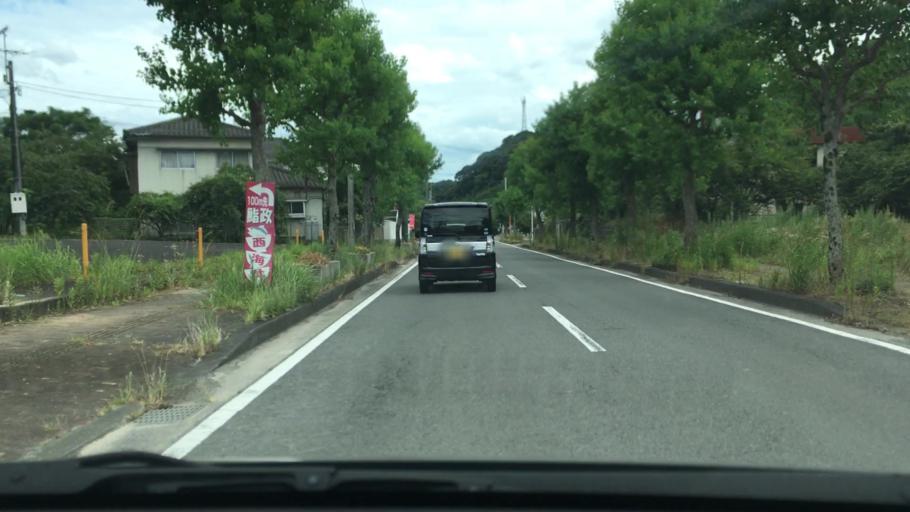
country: JP
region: Nagasaki
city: Sasebo
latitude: 32.9898
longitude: 129.7653
